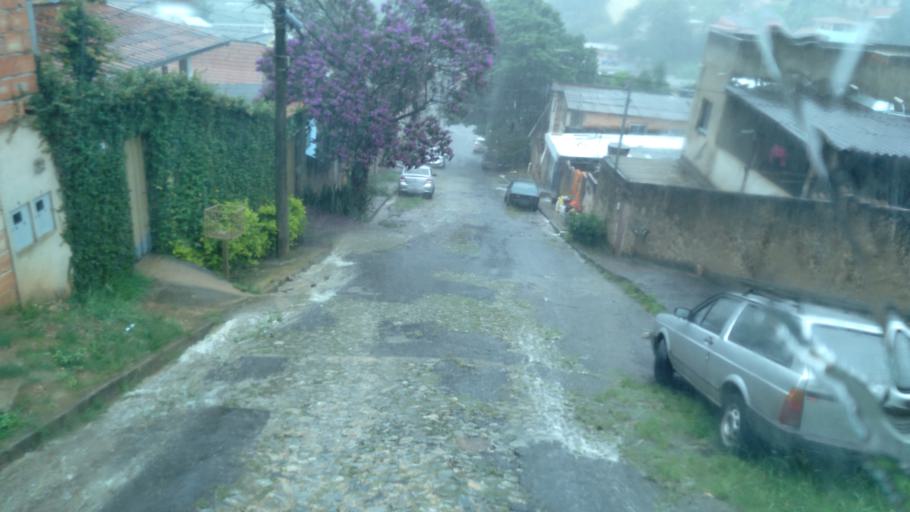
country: BR
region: Minas Gerais
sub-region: Belo Horizonte
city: Belo Horizonte
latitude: -19.9200
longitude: -43.8845
